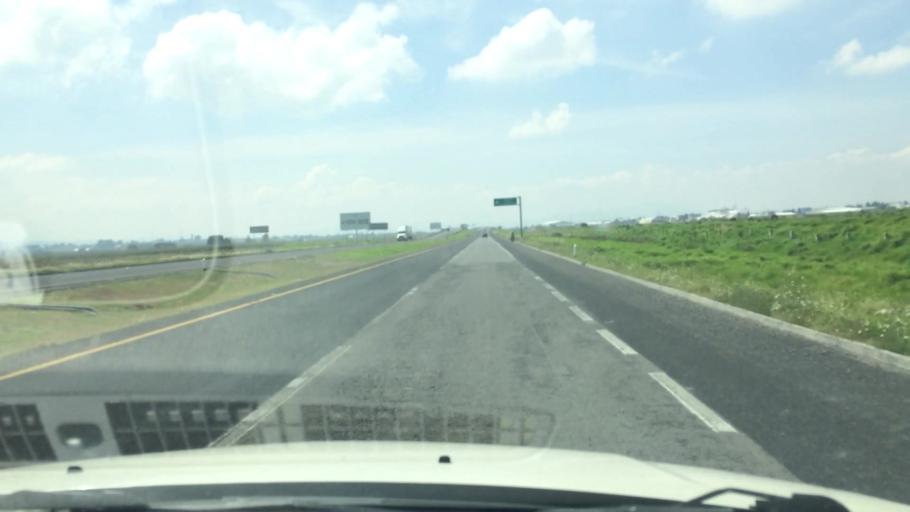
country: MX
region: Mexico
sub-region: Lerma
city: Colonia Isidro Fabela
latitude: 19.3145
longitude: -99.5220
